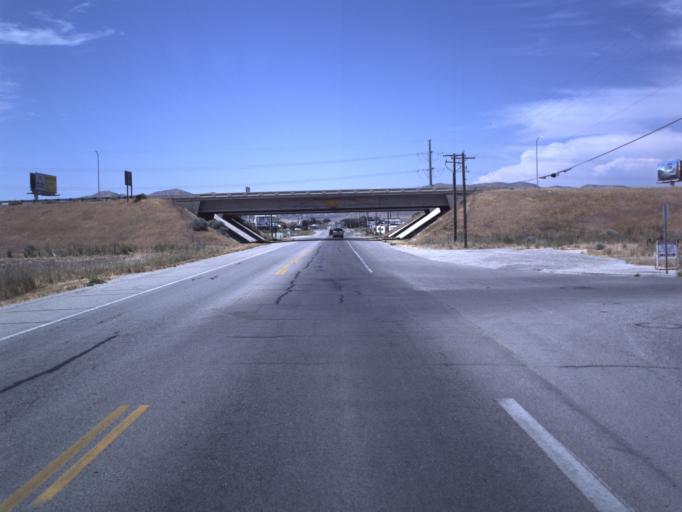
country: US
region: Utah
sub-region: Box Elder County
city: Tremonton
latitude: 41.7112
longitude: -112.1905
